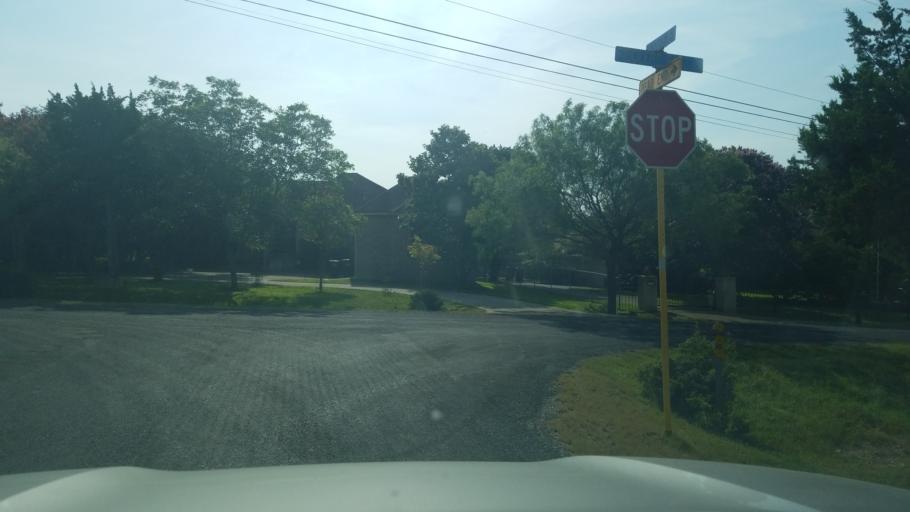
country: US
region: Texas
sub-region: Bexar County
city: Timberwood Park
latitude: 29.7008
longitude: -98.4957
